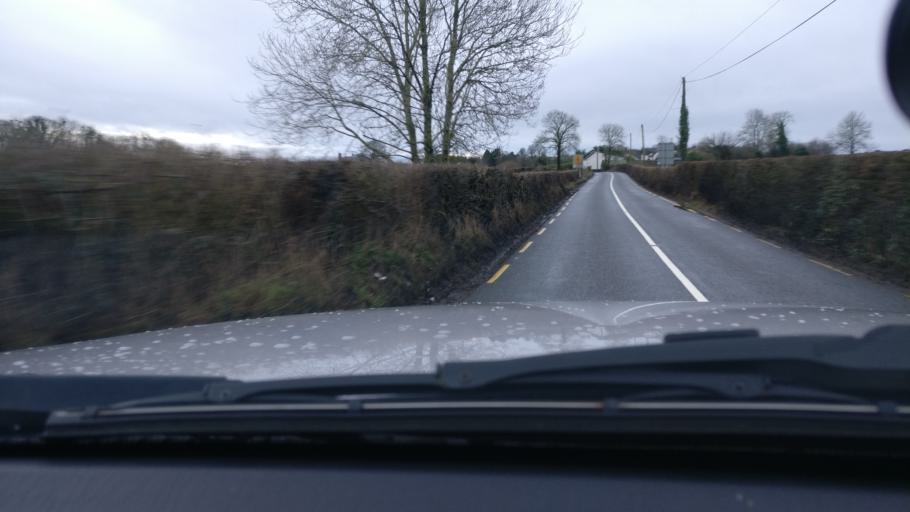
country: IE
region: Leinster
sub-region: An Longfort
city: Granard
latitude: 53.8102
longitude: -7.3746
